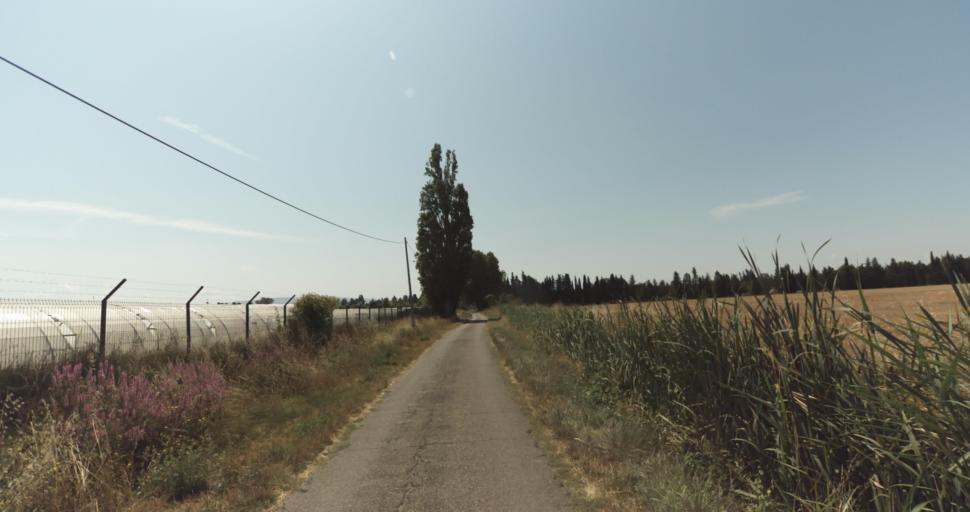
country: FR
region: Provence-Alpes-Cote d'Azur
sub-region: Departement du Vaucluse
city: Monteux
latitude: 44.0190
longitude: 5.0131
